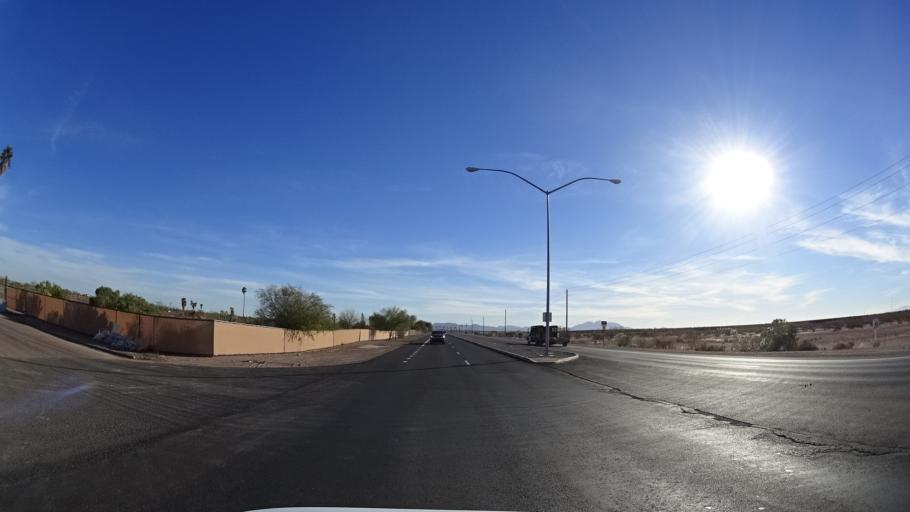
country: US
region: Arizona
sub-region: Maricopa County
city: Queen Creek
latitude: 33.3280
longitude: -111.6355
